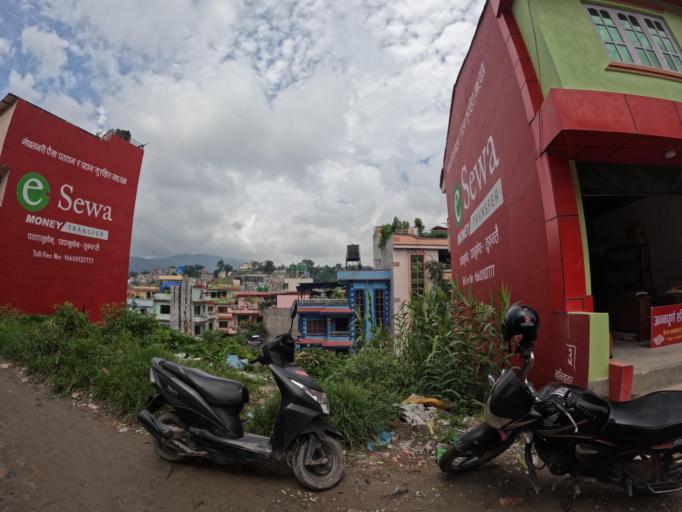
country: NP
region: Central Region
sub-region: Bagmati Zone
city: Kathmandu
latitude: 27.7525
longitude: 85.3177
